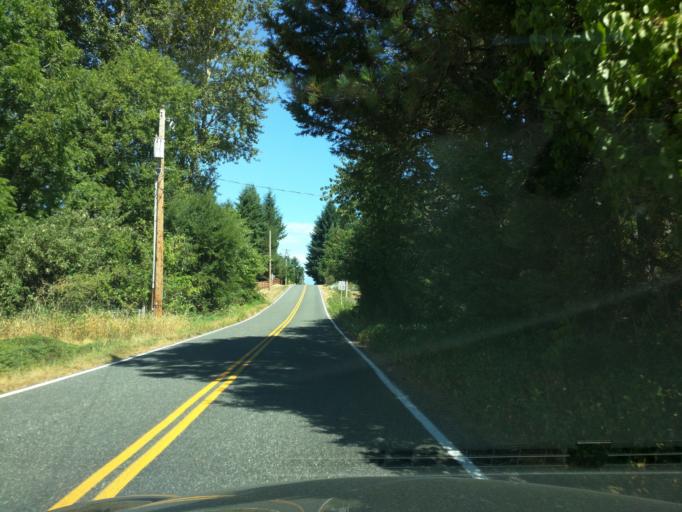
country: US
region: Washington
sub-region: Whatcom County
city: Lynden
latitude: 48.8775
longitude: -122.4148
